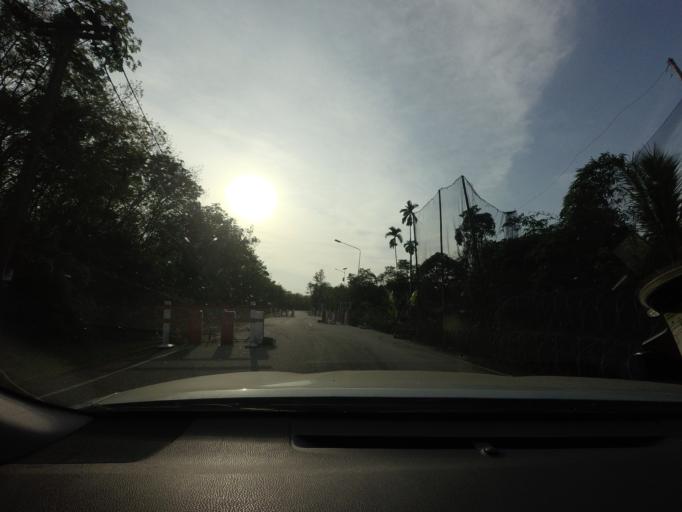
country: TH
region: Narathiwat
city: Ra-ngae
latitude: 6.3371
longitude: 101.7191
